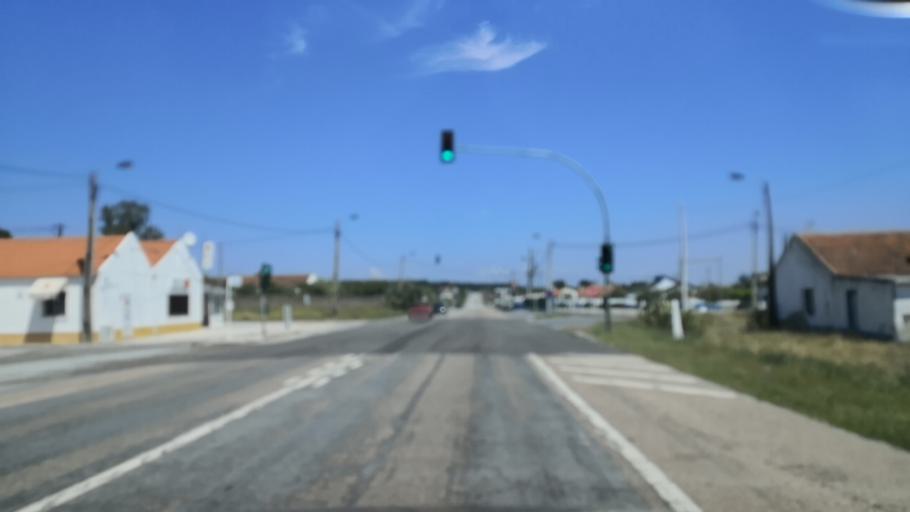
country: PT
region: Evora
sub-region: Vendas Novas
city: Vendas Novas
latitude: 38.6847
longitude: -8.5141
